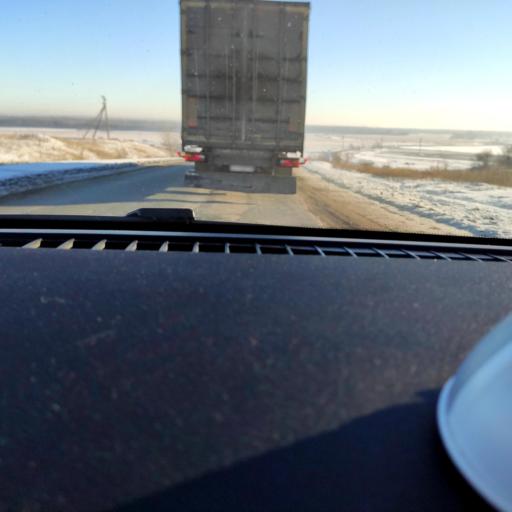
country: RU
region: Samara
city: Spiridonovka
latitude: 53.1445
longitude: 50.5825
